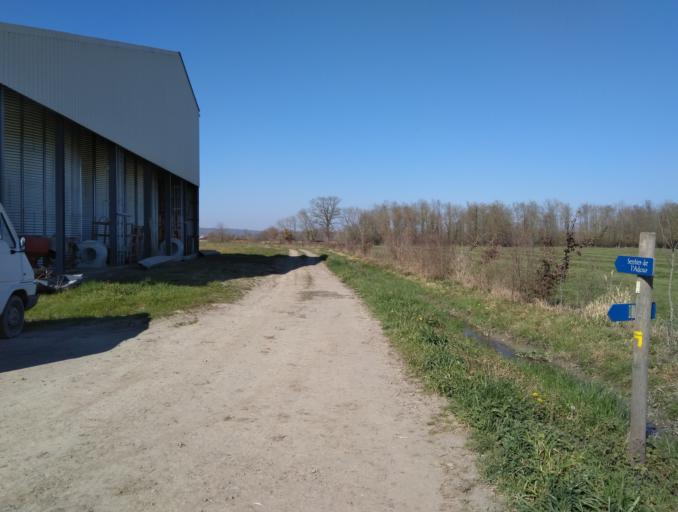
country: FR
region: Midi-Pyrenees
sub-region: Departement du Gers
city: Plaisance
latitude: 43.5435
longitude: 0.0090
